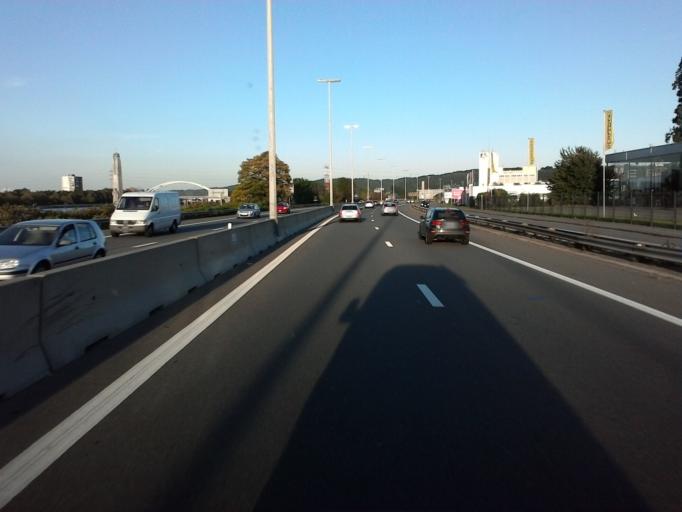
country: BE
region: Wallonia
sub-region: Province de Liege
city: Herstal
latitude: 50.6508
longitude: 5.6139
